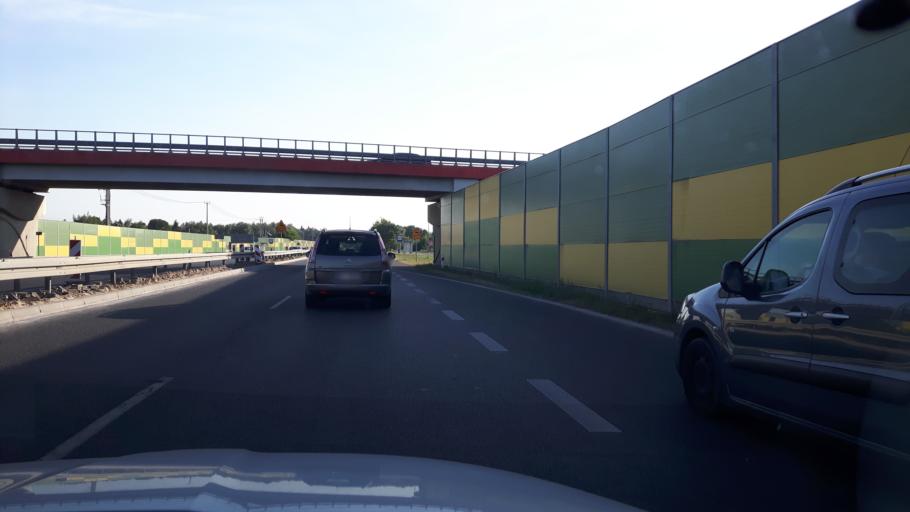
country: PL
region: Masovian Voivodeship
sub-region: Powiat legionowski
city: Serock
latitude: 52.4835
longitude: 21.0408
